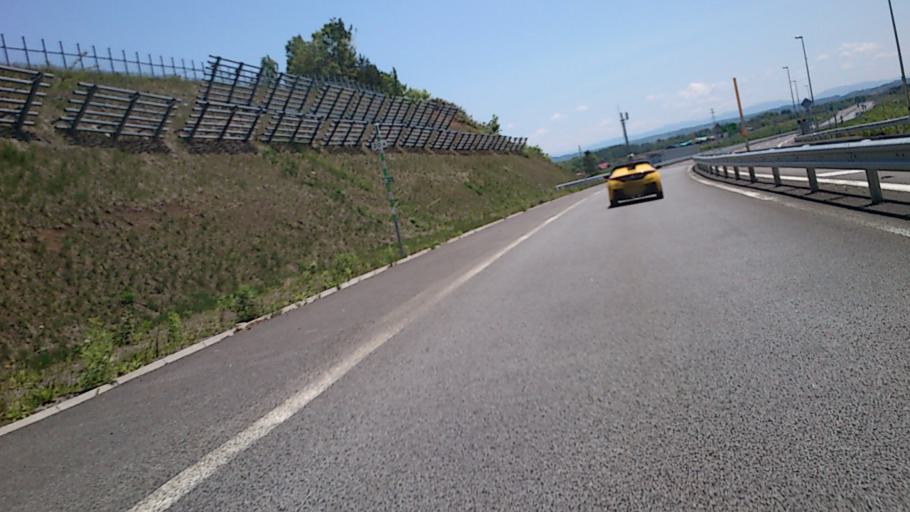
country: JP
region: Hokkaido
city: Nayoro
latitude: 44.4832
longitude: 142.3652
